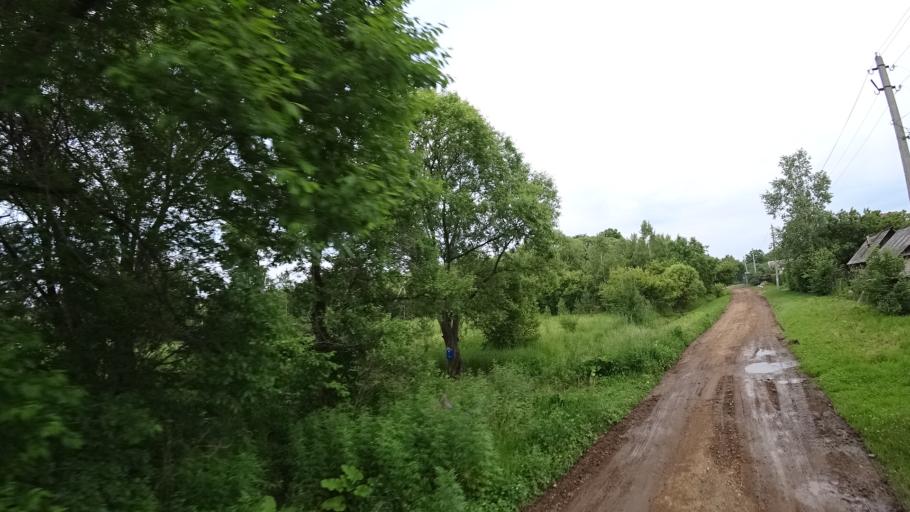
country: RU
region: Primorskiy
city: Novosysoyevka
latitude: 44.2407
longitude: 133.3773
